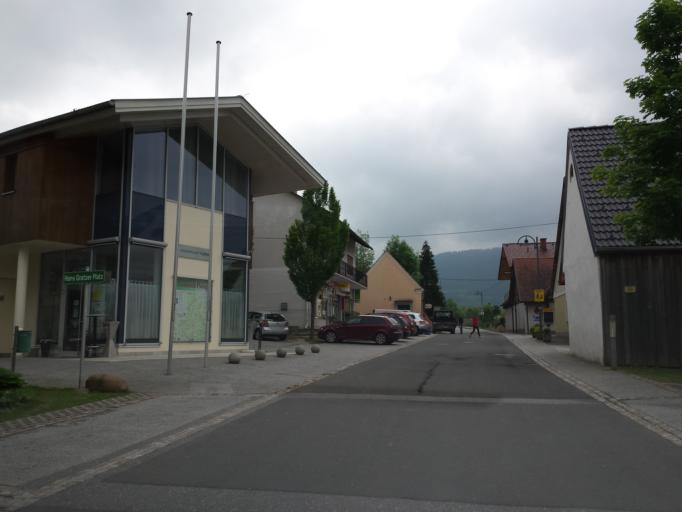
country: AT
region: Styria
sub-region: Politischer Bezirk Weiz
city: Floing
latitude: 47.2490
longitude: 15.7332
